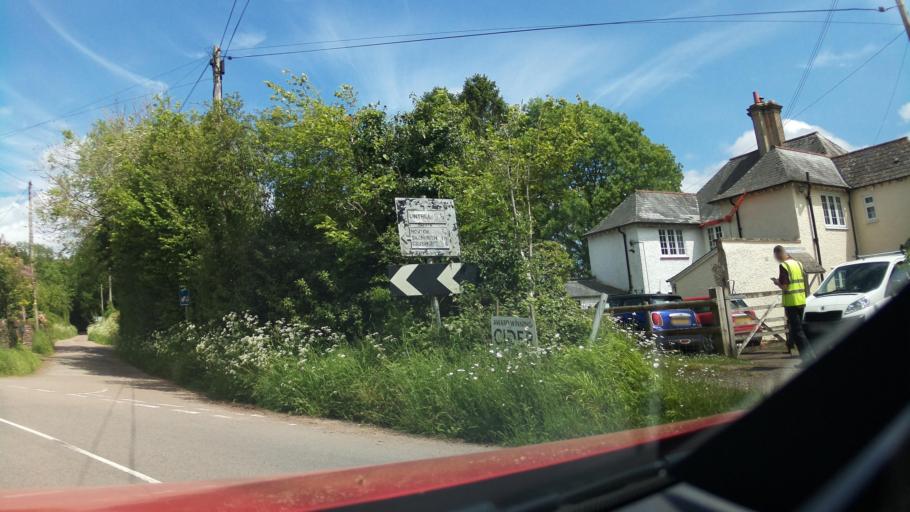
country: GB
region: England
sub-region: Herefordshire
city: Llanrothal
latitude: 51.8683
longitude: -2.8019
